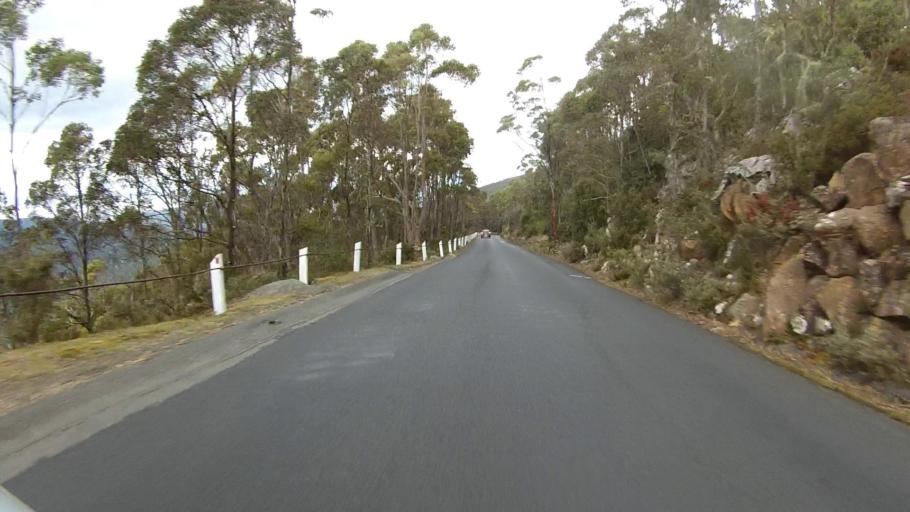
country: AU
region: Tasmania
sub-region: Glenorchy
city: West Moonah
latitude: -42.8978
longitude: 147.2440
